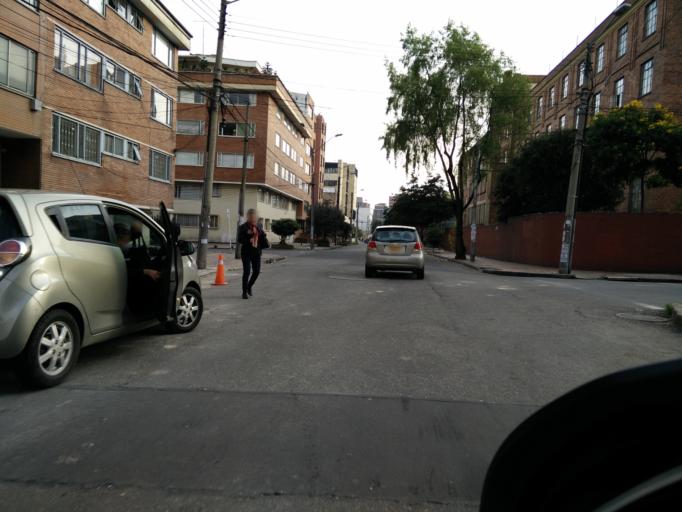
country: CO
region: Bogota D.C.
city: Barrio San Luis
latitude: 4.6504
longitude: -74.0615
